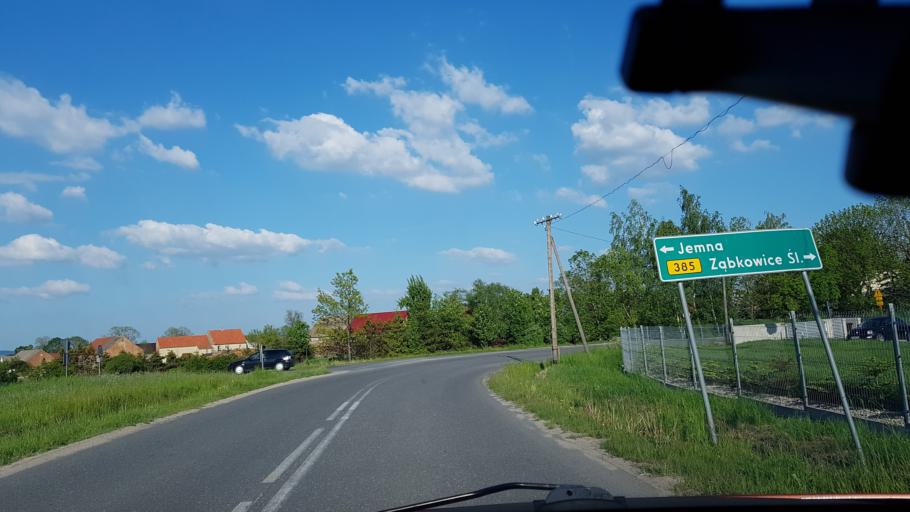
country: PL
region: Lower Silesian Voivodeship
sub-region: Powiat zabkowicki
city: Budzow
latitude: 50.5755
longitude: 16.6780
